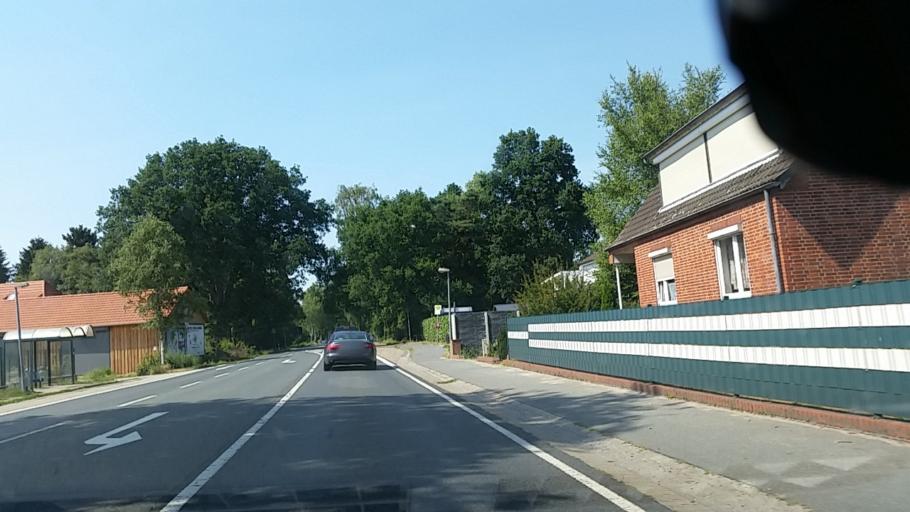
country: DE
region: Lower Saxony
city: Ottersberg
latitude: 53.0716
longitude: 9.1663
